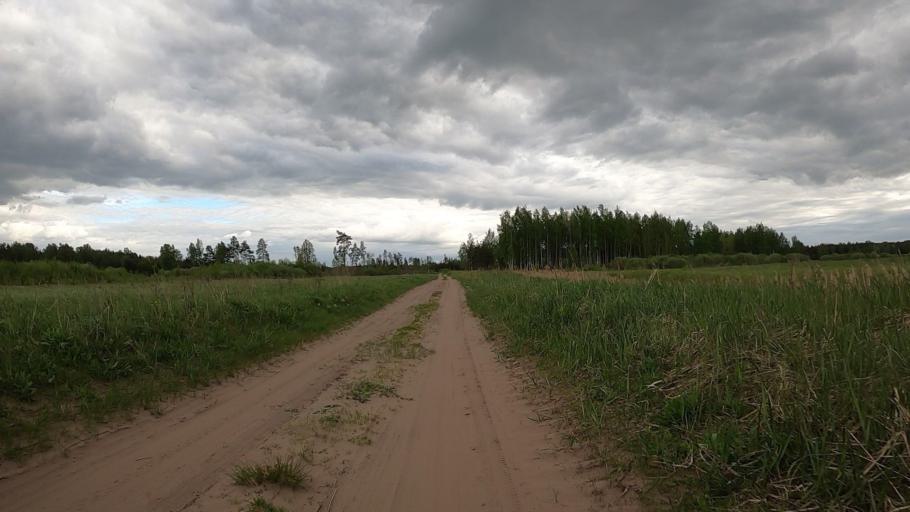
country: LV
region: Ozolnieku
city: Ozolnieki
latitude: 56.8119
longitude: 23.7779
